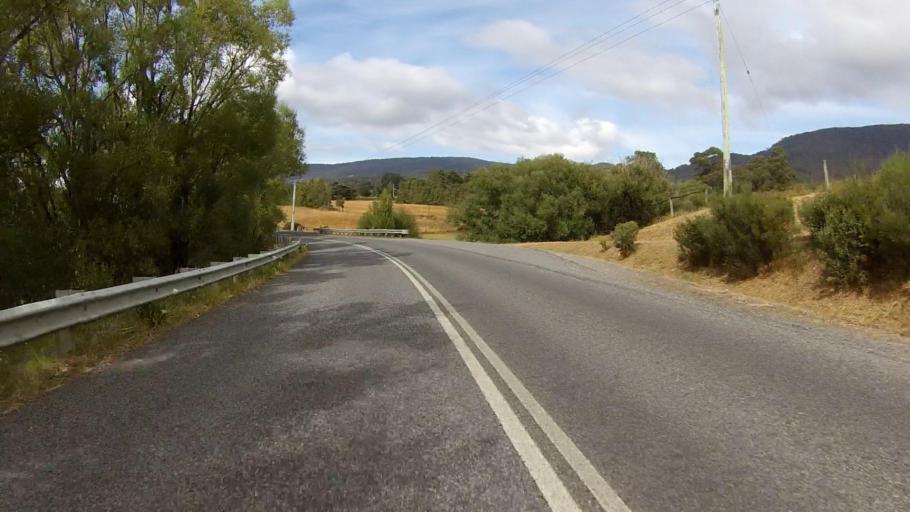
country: AU
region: Tasmania
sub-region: Kingborough
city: Kettering
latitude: -43.1537
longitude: 147.2381
